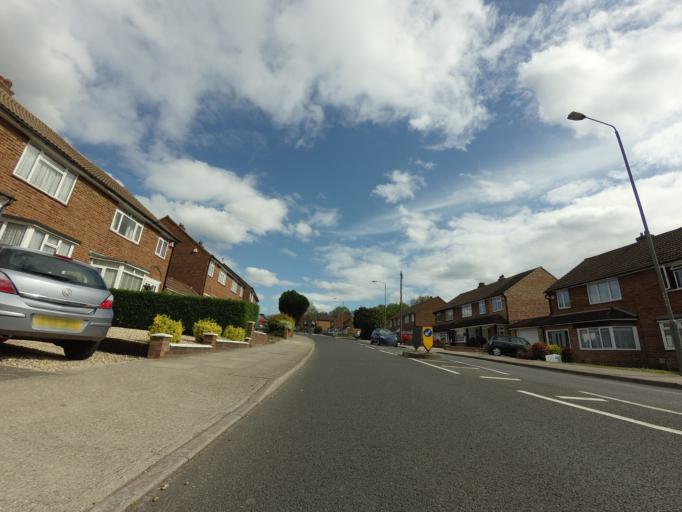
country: GB
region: England
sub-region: Greater London
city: Orpington
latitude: 51.3706
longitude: 0.1145
